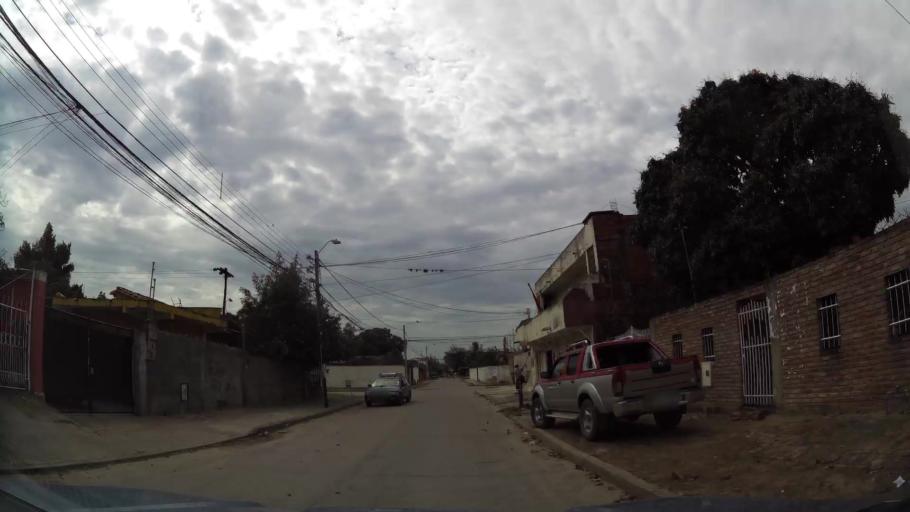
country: BO
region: Santa Cruz
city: Santa Cruz de la Sierra
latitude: -17.7489
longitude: -63.1911
